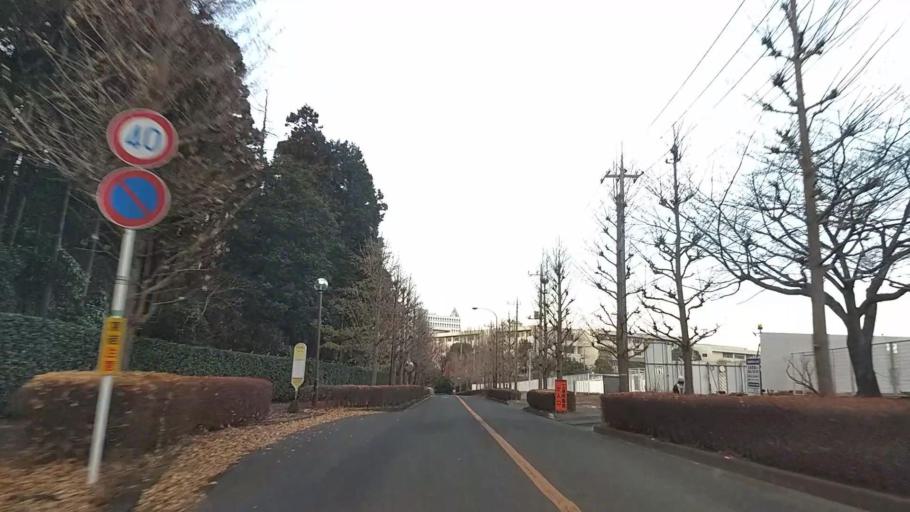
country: JP
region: Kanagawa
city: Atsugi
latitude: 35.4466
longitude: 139.3142
